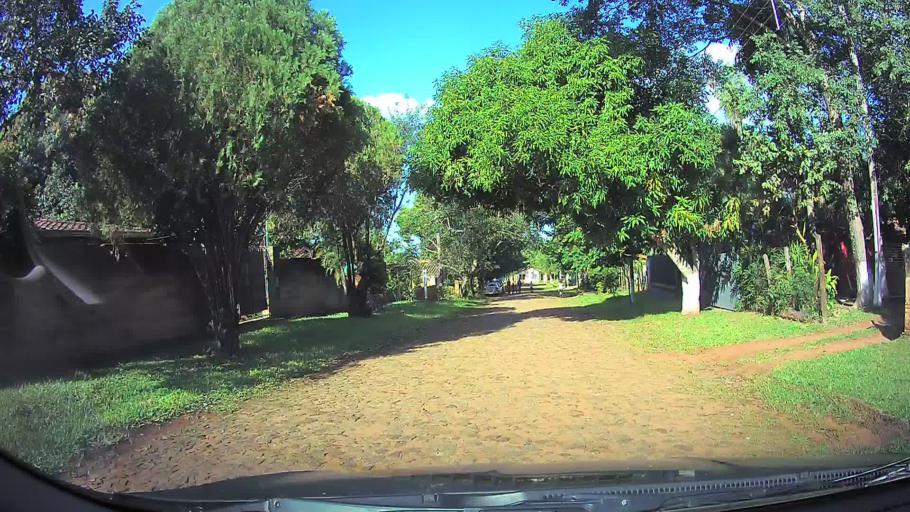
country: PY
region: Central
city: Capiata
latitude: -25.2788
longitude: -57.4580
